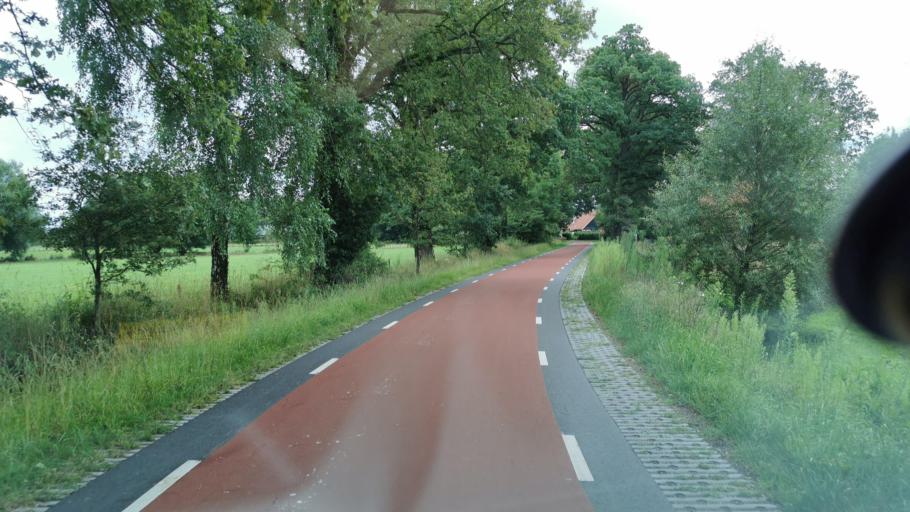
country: NL
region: Overijssel
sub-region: Gemeente Losser
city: Losser
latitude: 52.2536
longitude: 6.9849
